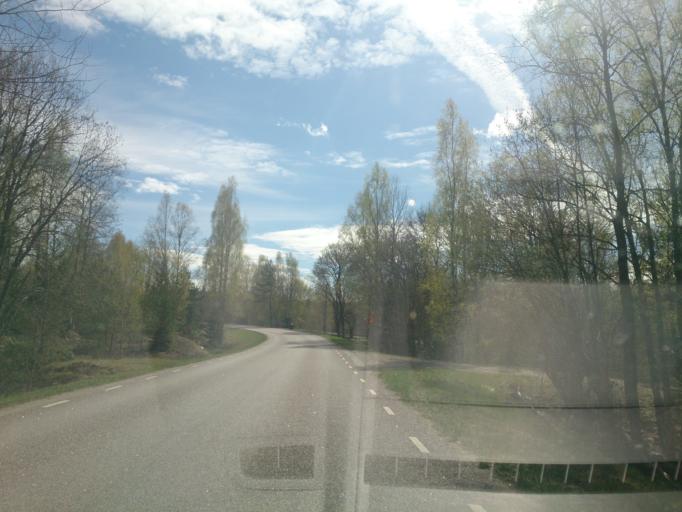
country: SE
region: OEstergoetland
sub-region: Atvidabergs Kommun
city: Atvidaberg
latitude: 58.2678
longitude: 16.0336
